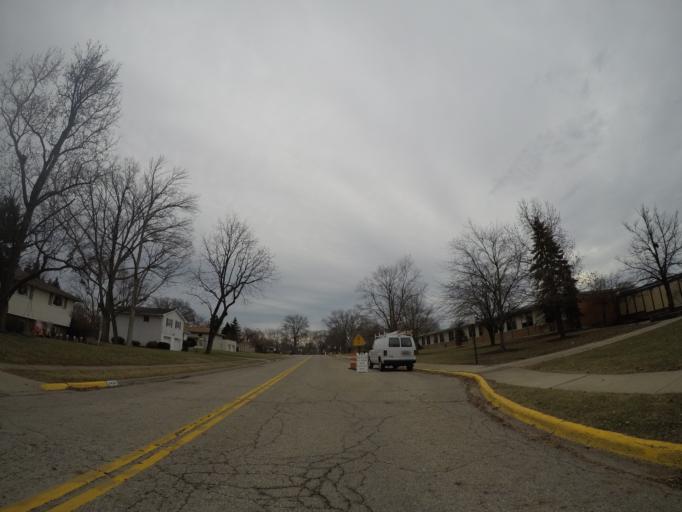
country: US
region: Ohio
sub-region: Franklin County
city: Upper Arlington
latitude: 40.0393
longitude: -83.0824
